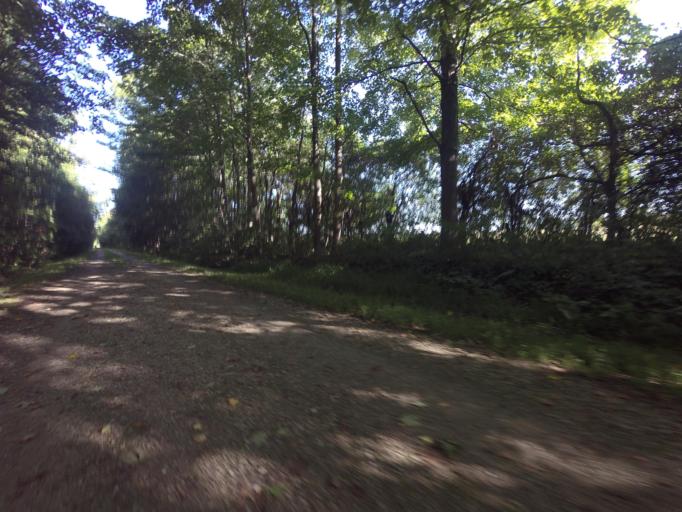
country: CA
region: Ontario
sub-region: Wellington County
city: Guelph
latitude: 43.6561
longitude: -80.4234
